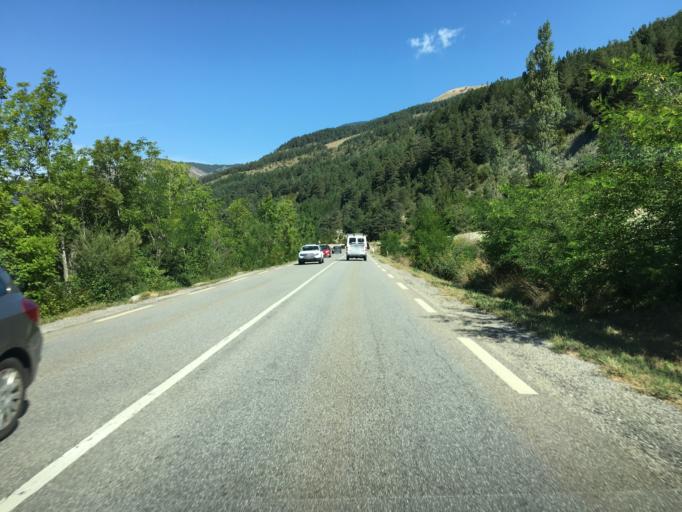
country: FR
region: Provence-Alpes-Cote d'Azur
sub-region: Departement des Hautes-Alpes
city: Veynes
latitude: 44.5591
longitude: 5.7658
